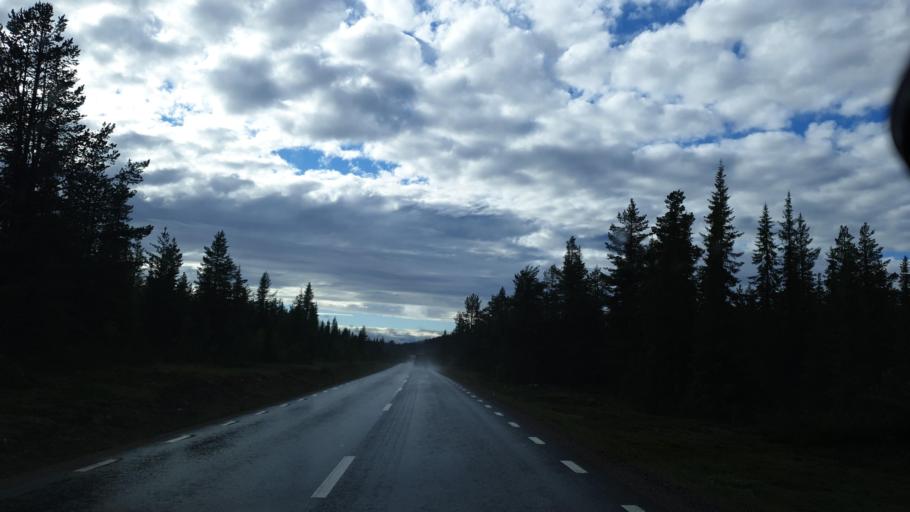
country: SE
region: Norrbotten
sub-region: Arjeplogs Kommun
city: Arjeplog
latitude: 65.9149
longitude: 18.3305
